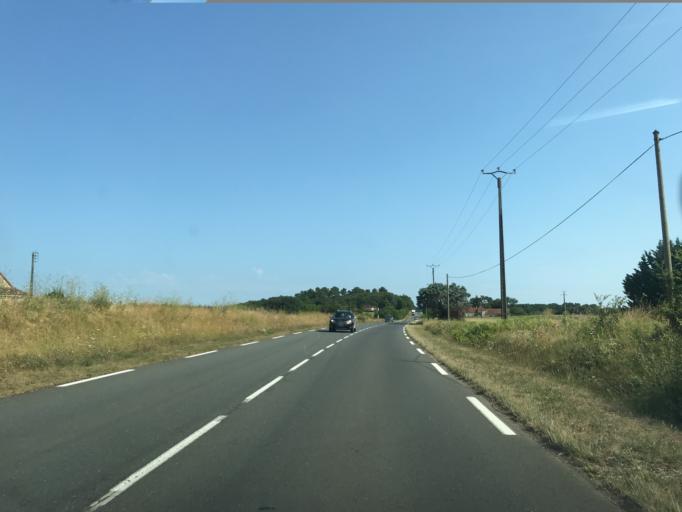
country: FR
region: Aquitaine
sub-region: Departement de la Dordogne
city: Sarlat-la-Caneda
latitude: 44.9739
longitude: 1.2373
